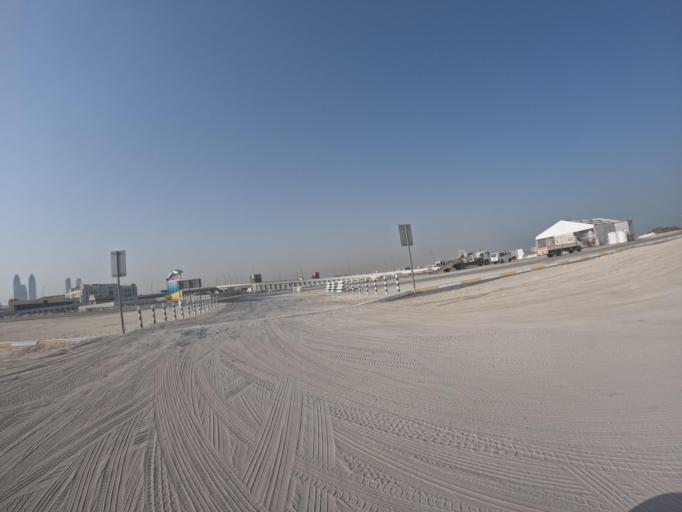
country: AE
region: Dubai
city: Dubai
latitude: 25.1958
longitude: 55.2448
